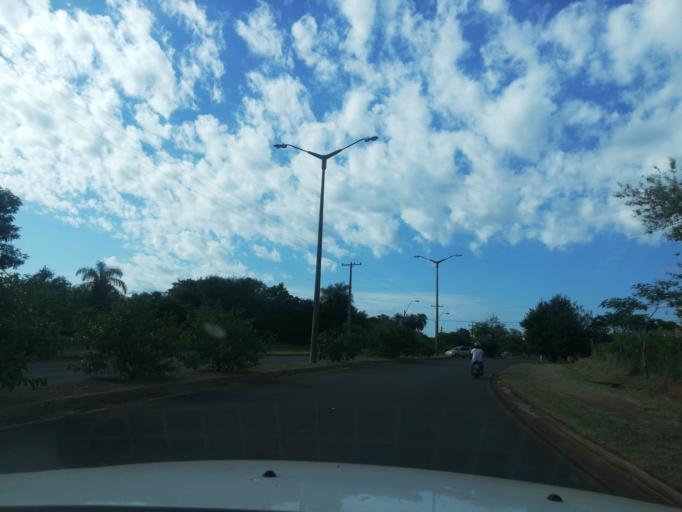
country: PY
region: Itapua
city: Encarnacion
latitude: -27.3477
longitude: -55.8490
